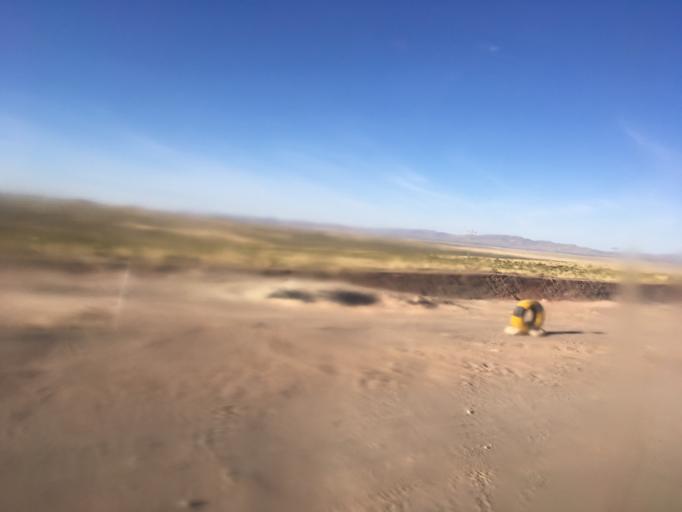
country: PE
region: Puno
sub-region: Provincia de Chucuito
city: Kelluyo
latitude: -16.9829
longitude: -69.0300
